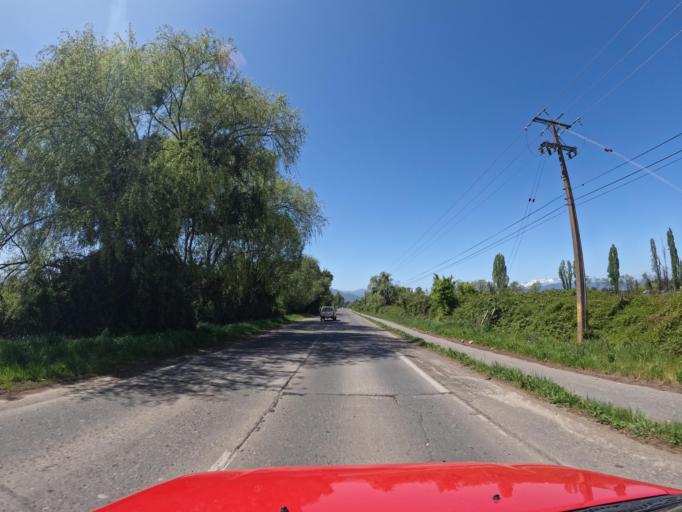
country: CL
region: Maule
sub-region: Provincia de Linares
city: Linares
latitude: -35.8288
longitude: -71.5009
